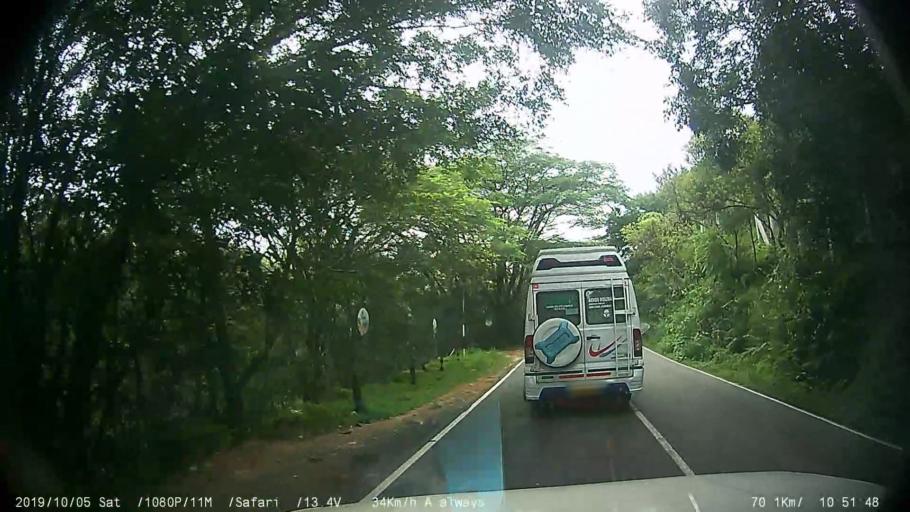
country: IN
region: Kerala
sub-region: Kottayam
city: Erattupetta
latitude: 9.5679
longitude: 76.9769
